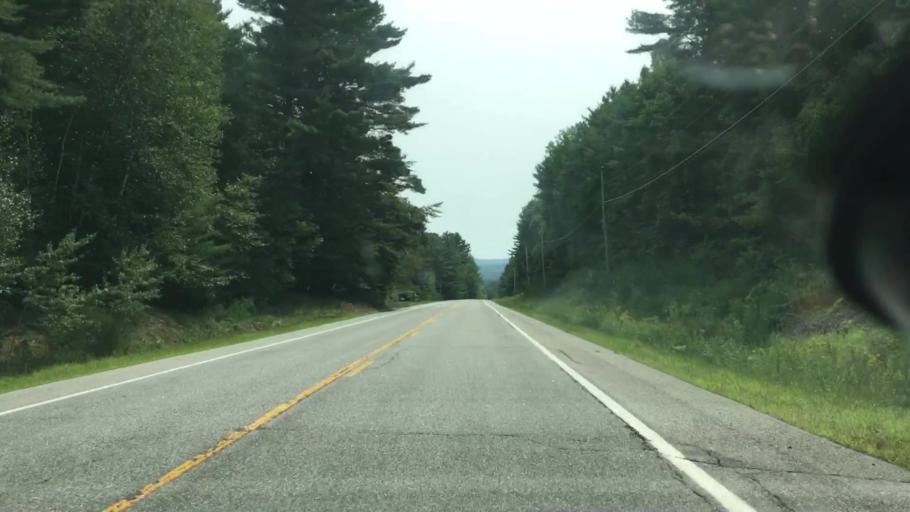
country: US
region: Maine
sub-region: Kennebec County
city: Wayne
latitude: 44.3760
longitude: -70.0982
